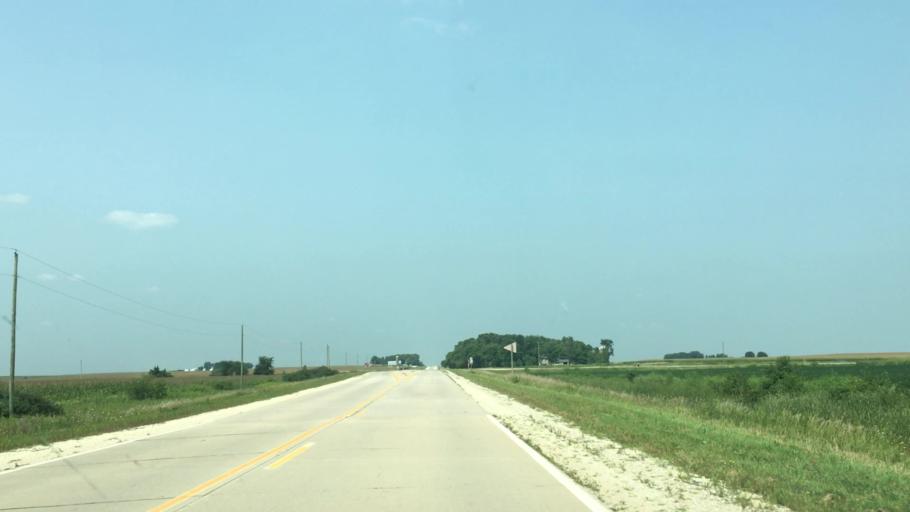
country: US
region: Iowa
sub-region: Fayette County
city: Fayette
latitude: 42.7571
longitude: -91.8043
